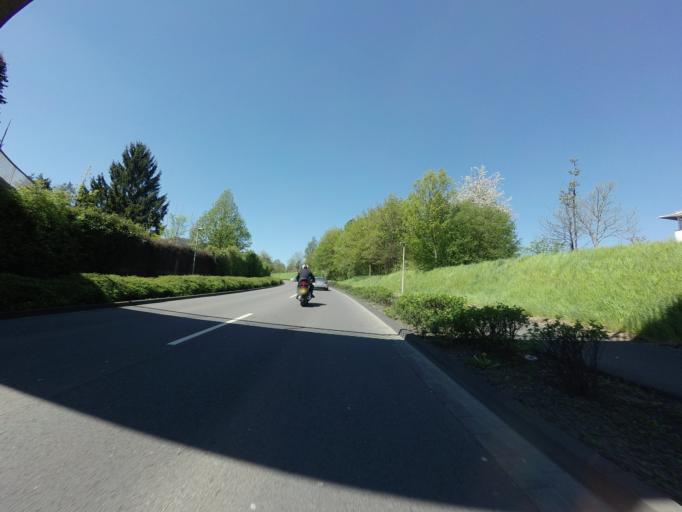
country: DE
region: North Rhine-Westphalia
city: Kreuztal
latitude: 50.9624
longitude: 7.9941
